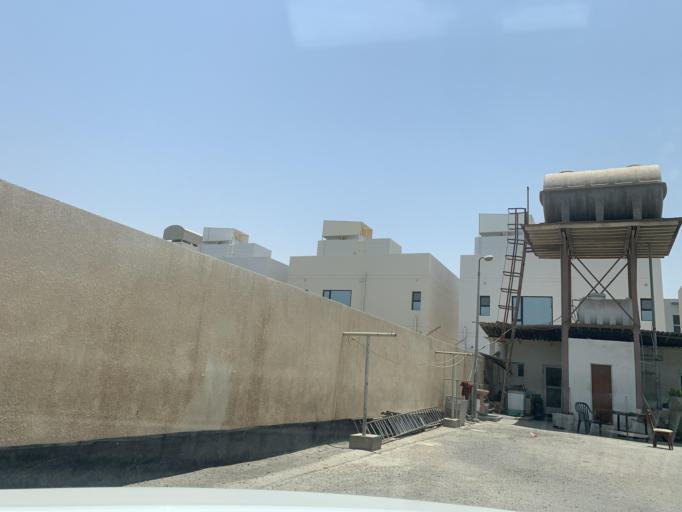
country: BH
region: Manama
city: Jidd Hafs
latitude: 26.2144
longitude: 50.4692
